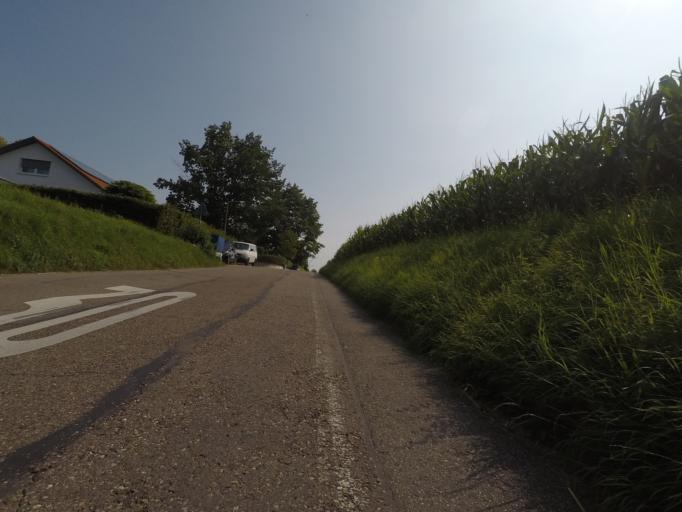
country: DE
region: Baden-Wuerttemberg
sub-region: Regierungsbezirk Stuttgart
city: Schorndorf
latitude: 48.7956
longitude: 9.5044
